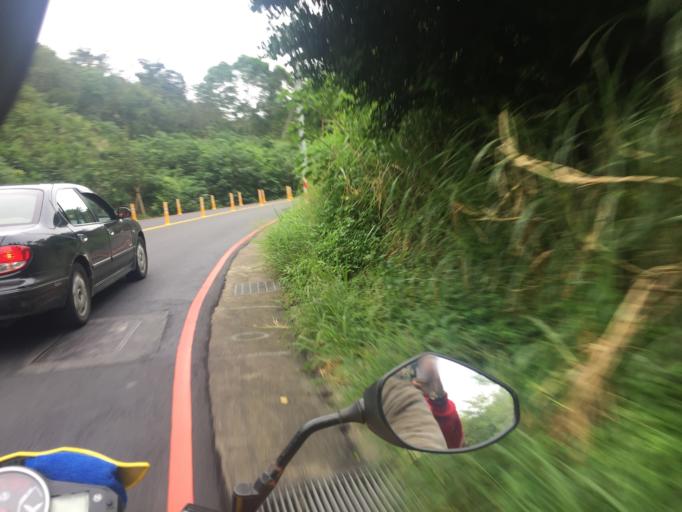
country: TW
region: Taiwan
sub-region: Hsinchu
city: Hsinchu
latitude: 24.7905
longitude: 120.9571
